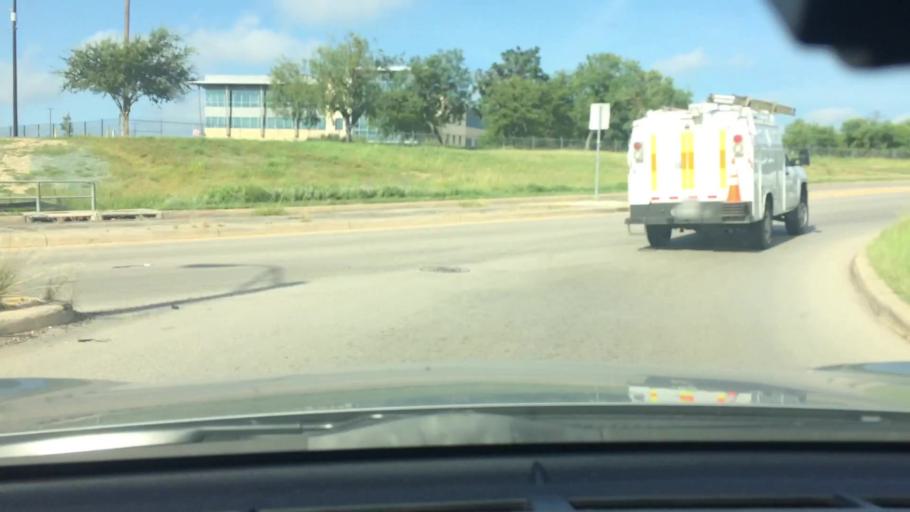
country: US
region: Texas
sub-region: Bexar County
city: China Grove
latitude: 29.3728
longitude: -98.3954
